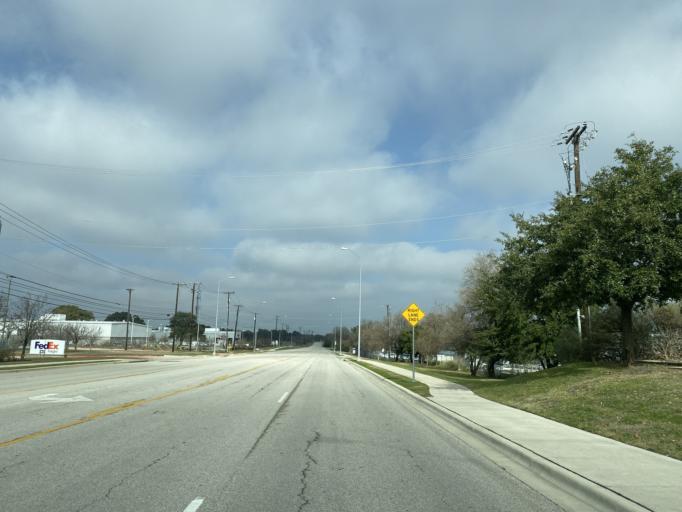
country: US
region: Texas
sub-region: Williamson County
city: Round Rock
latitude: 30.5411
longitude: -97.6948
